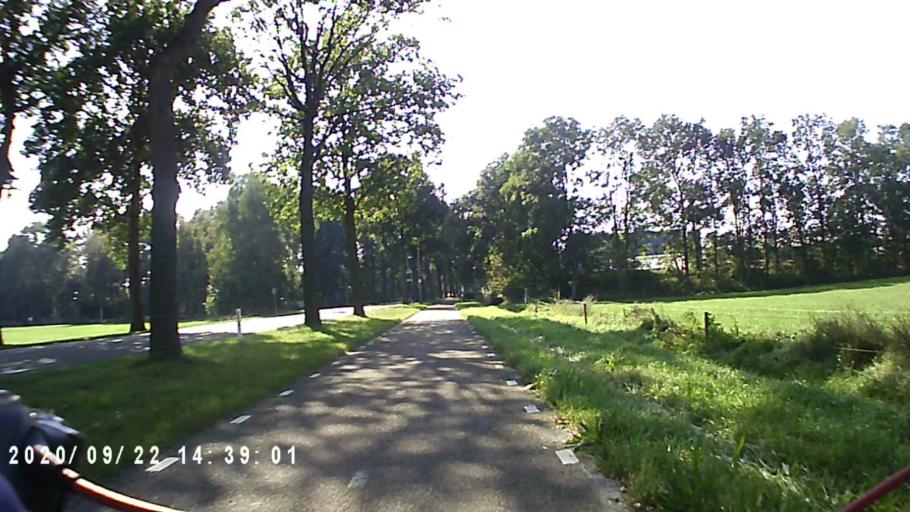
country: NL
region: Groningen
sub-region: Gemeente Leek
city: Leek
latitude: 53.0251
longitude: 6.3515
